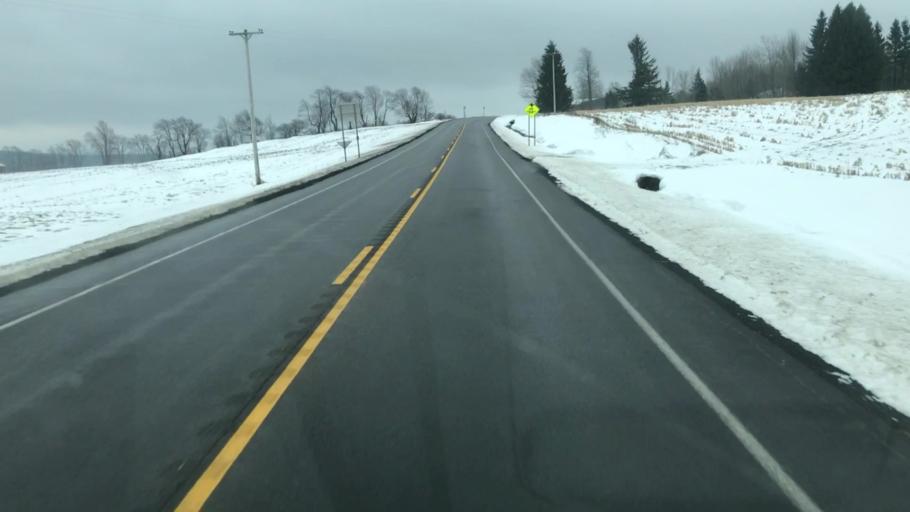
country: US
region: New York
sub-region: Cayuga County
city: Moravia
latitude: 42.7712
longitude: -76.3336
